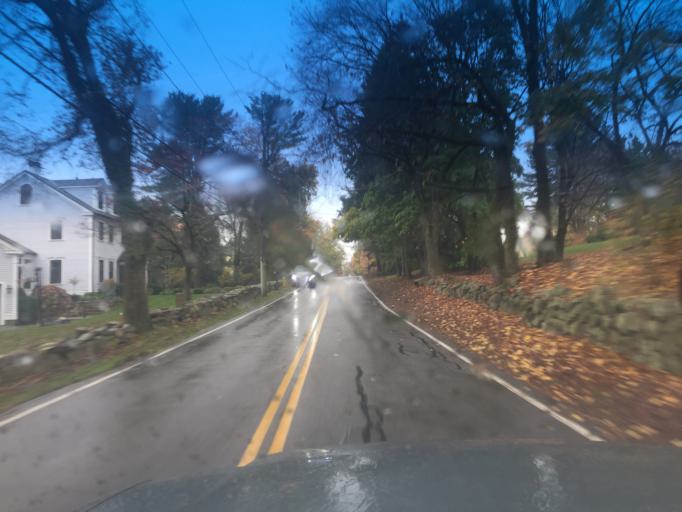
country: US
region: Massachusetts
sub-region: Norfolk County
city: Westwood
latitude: 42.2198
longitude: -71.2024
